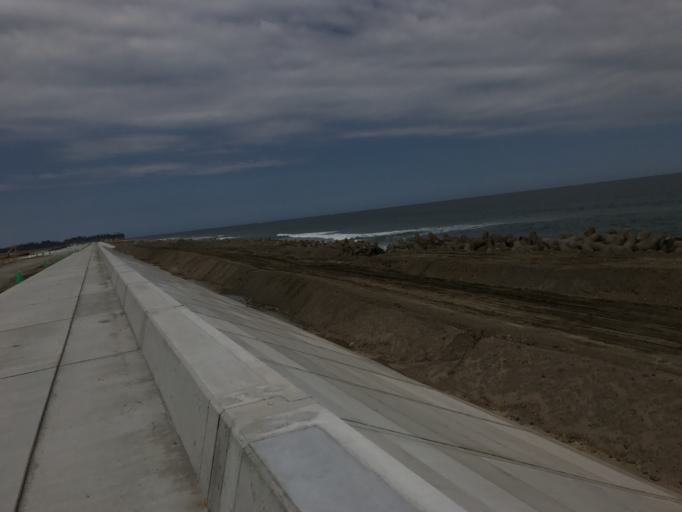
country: JP
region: Miyagi
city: Marumori
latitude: 37.7981
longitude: 140.9859
